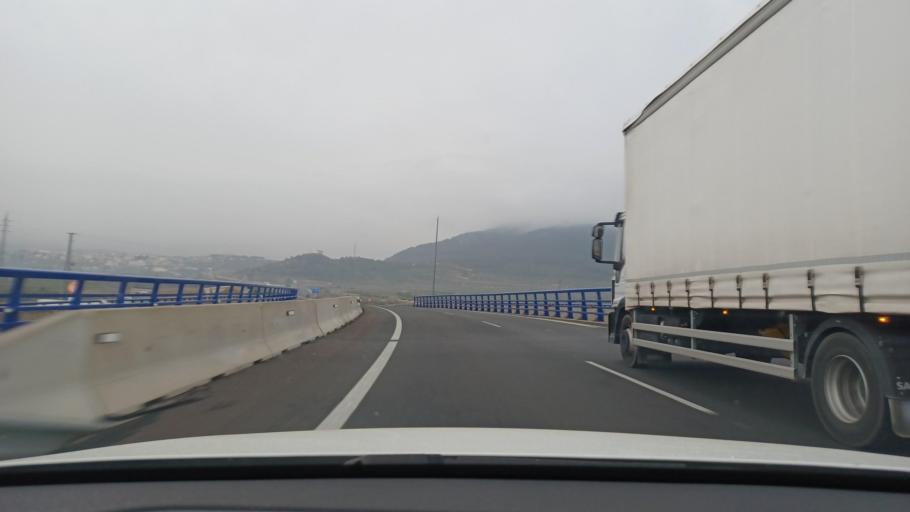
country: ES
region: Valencia
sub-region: Provincia de Valencia
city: La Font de la Figuera
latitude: 38.8276
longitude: -0.8924
